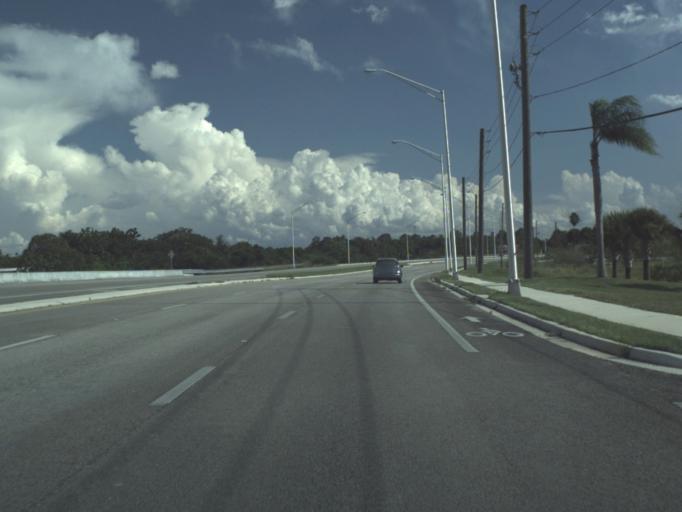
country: US
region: Florida
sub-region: Highlands County
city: Avon Park
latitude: 27.6327
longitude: -81.5176
